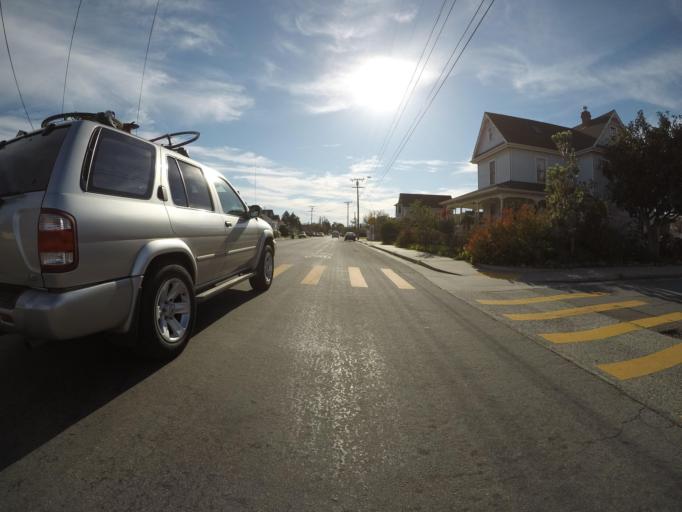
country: US
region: California
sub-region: Santa Cruz County
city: Santa Cruz
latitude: 36.9628
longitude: -122.0405
